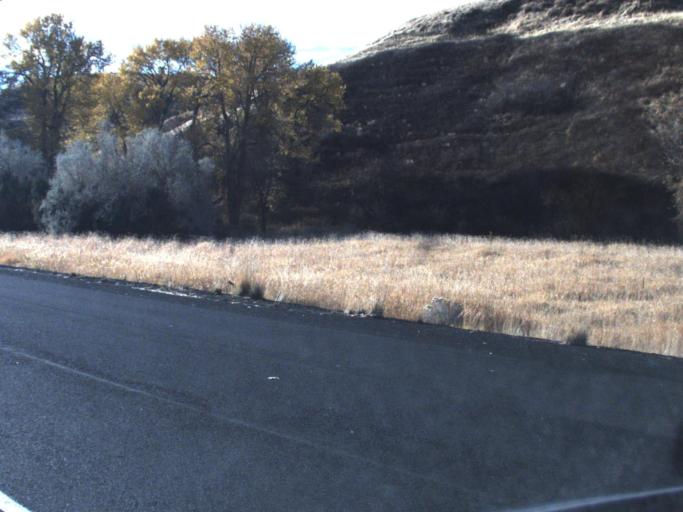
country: US
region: Washington
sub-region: Garfield County
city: Pomeroy
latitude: 46.4503
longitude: -117.4697
